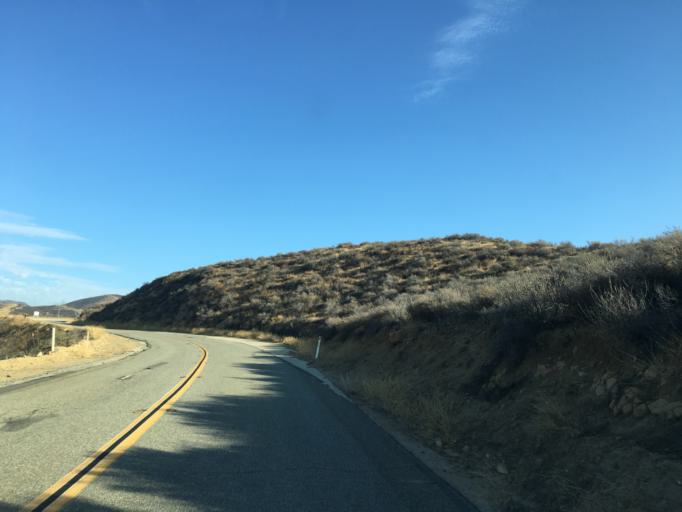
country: US
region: California
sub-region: Los Angeles County
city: Castaic
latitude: 34.5447
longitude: -118.6521
